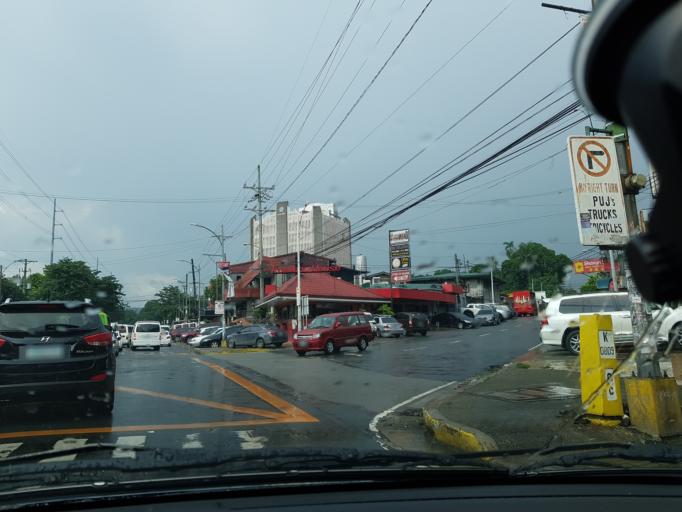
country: PH
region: Calabarzon
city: Del Monte
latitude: 14.6387
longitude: 121.0260
